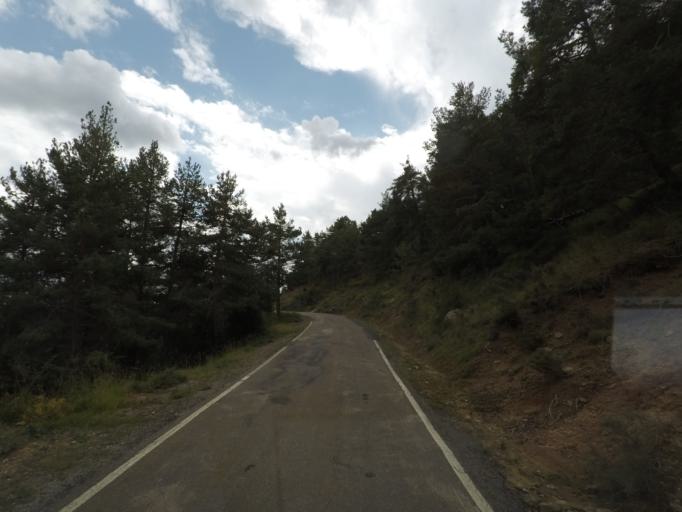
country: ES
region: Aragon
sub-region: Provincia de Huesca
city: Boltana
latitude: 42.4039
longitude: -0.0299
